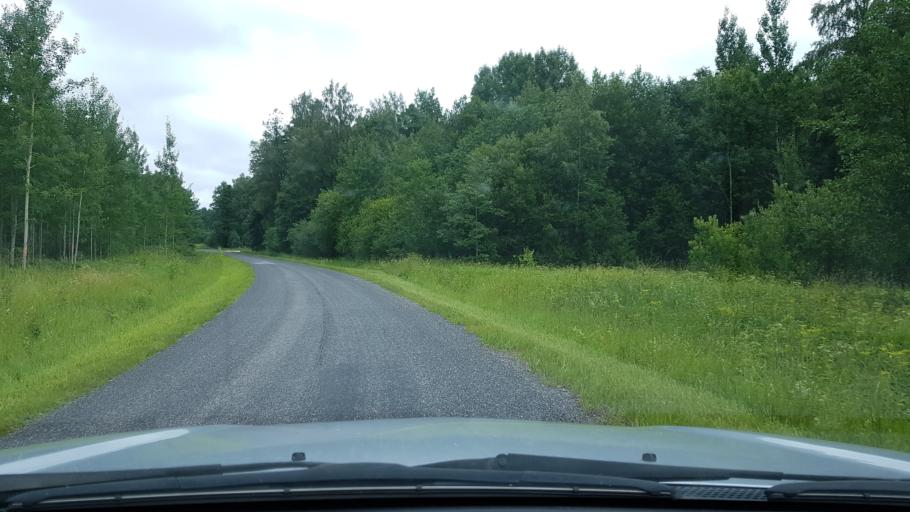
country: EE
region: Ida-Virumaa
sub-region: Narva-Joesuu linn
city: Narva-Joesuu
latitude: 59.3532
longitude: 28.0367
